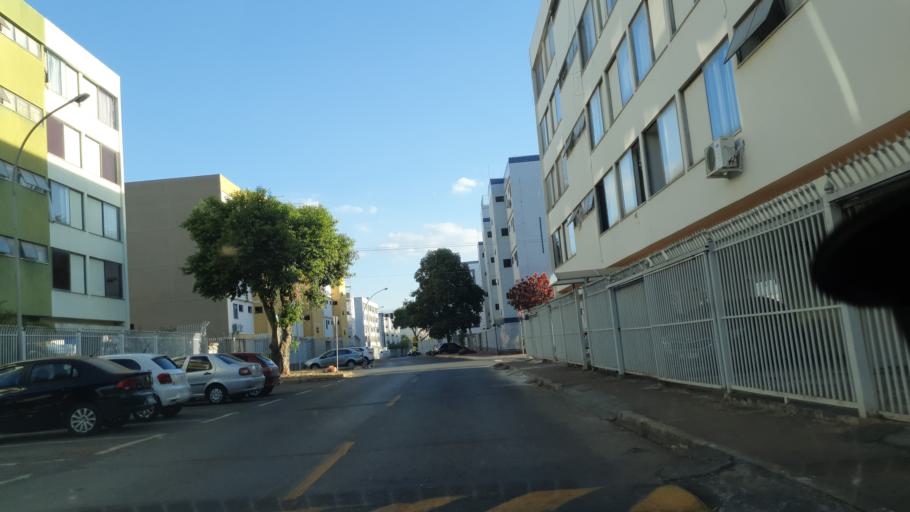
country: BR
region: Federal District
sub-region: Brasilia
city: Brasilia
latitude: -15.7974
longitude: -47.9417
